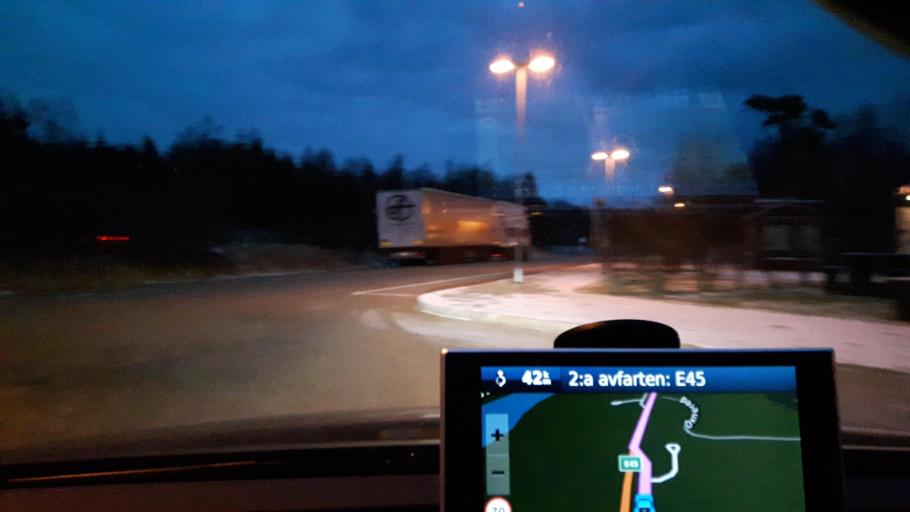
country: SE
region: Vaestra Goetaland
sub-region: Vanersborgs Kommun
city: Vanersborg
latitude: 58.3646
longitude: 12.2647
